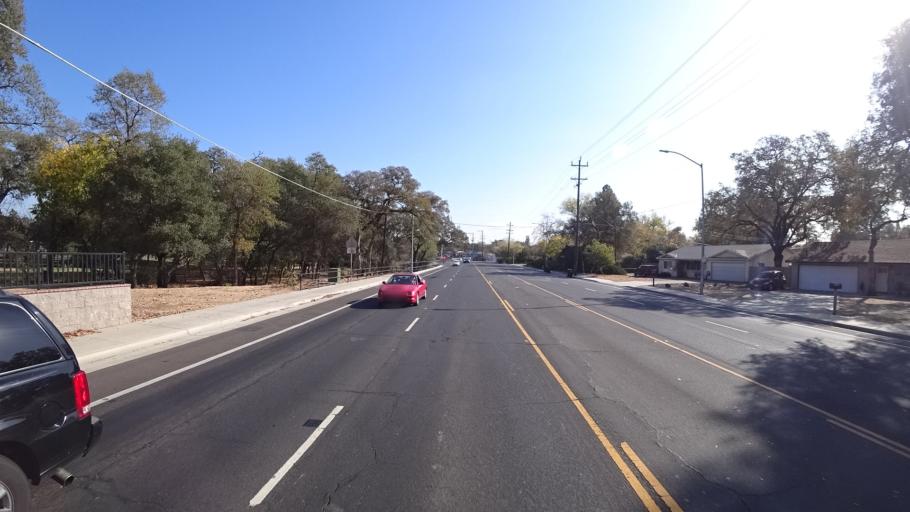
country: US
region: California
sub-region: Sacramento County
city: Citrus Heights
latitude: 38.7071
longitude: -121.2933
